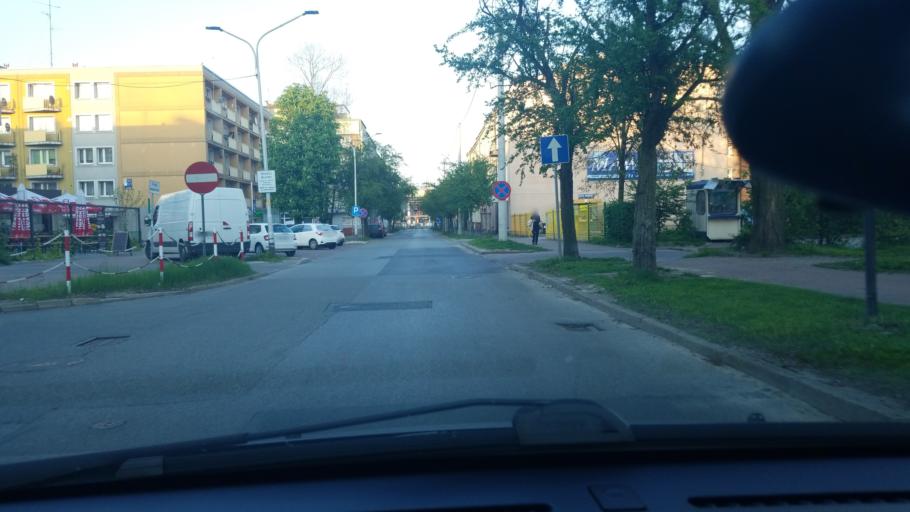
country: PL
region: Silesian Voivodeship
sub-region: Czestochowa
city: Czestochowa
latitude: 50.8087
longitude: 19.1149
